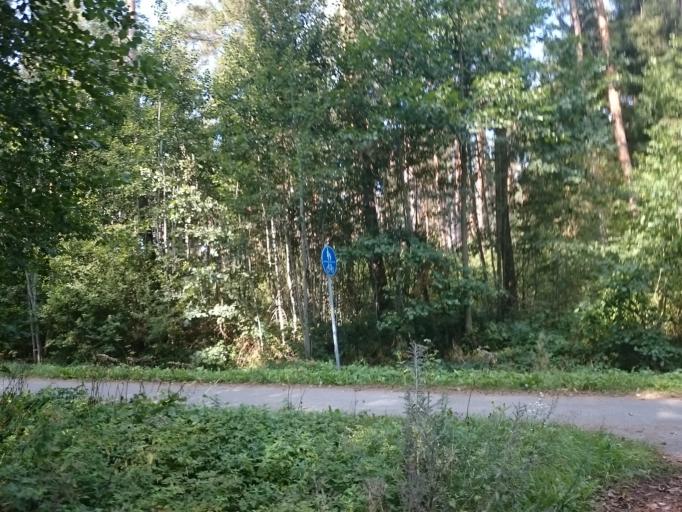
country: DE
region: Bavaria
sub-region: Regierungsbezirk Mittelfranken
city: Hilpoltstein
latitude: 49.1631
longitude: 11.1654
